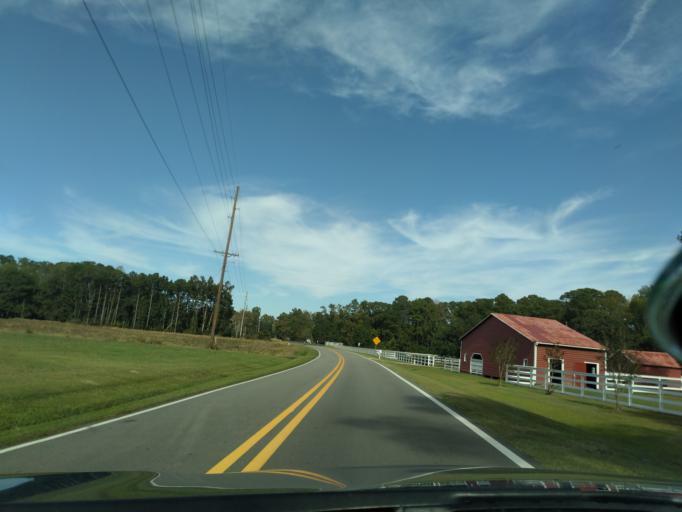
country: US
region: North Carolina
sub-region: Beaufort County
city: River Road
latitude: 35.5085
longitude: -76.9676
